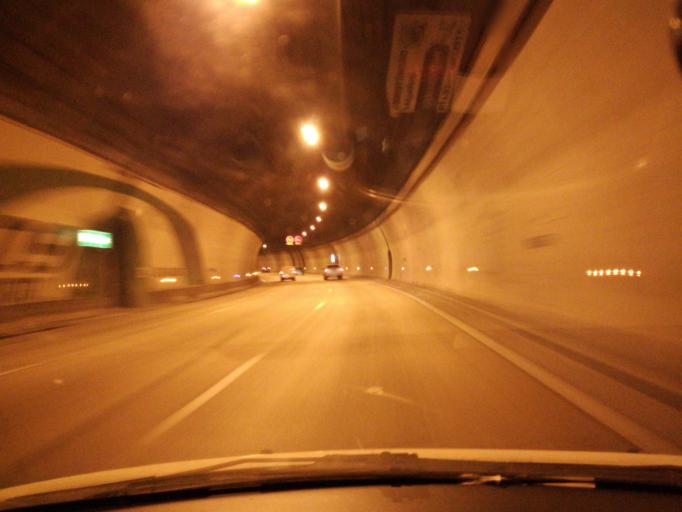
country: FR
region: Provence-Alpes-Cote d'Azur
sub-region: Departement des Alpes-Maritimes
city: Falicon
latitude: 43.7328
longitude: 7.2557
